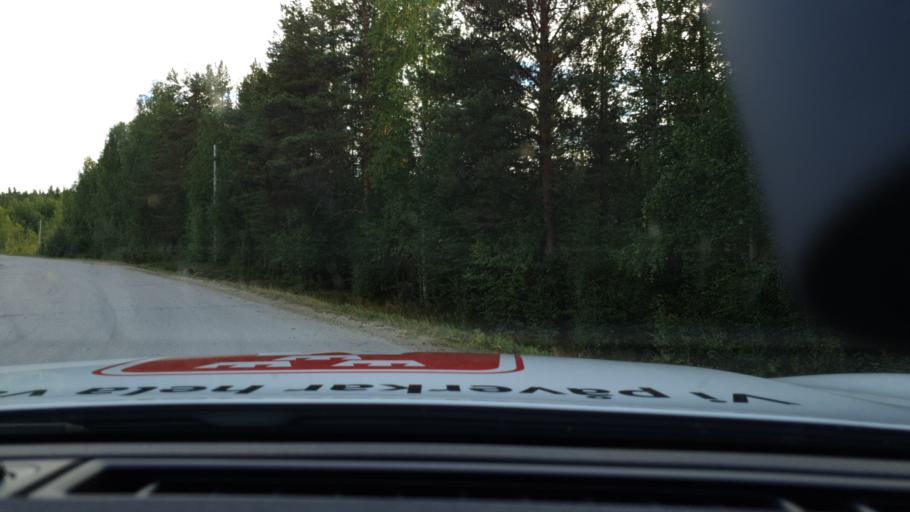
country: SE
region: Norrbotten
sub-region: Overkalix Kommun
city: OEverkalix
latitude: 66.6457
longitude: 22.1975
